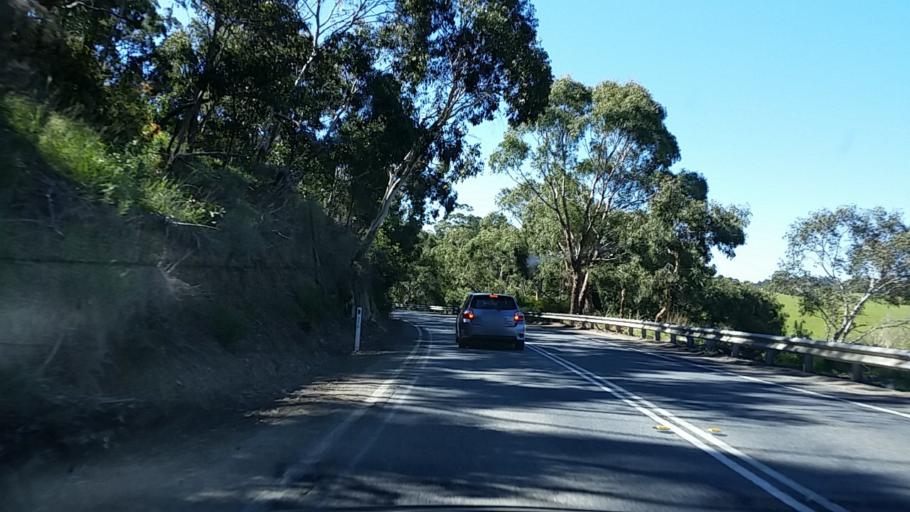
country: AU
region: South Australia
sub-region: Mount Barker
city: Meadows
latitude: -35.1868
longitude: 138.7718
